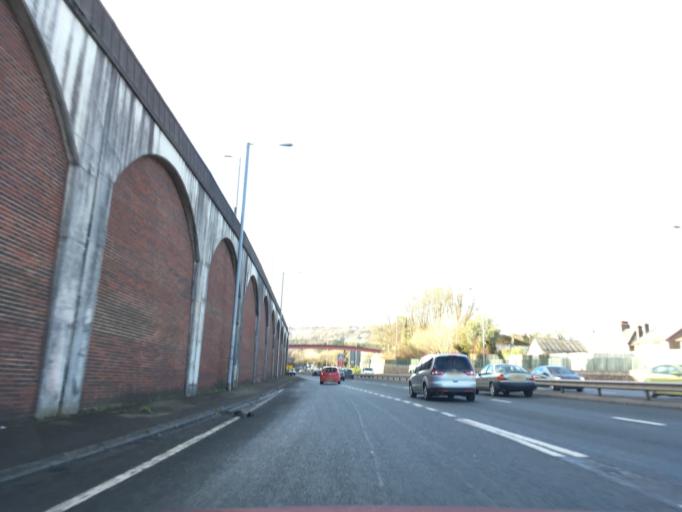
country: GB
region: Wales
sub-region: Torfaen County Borough
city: Pontypool
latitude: 51.6981
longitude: -3.0329
